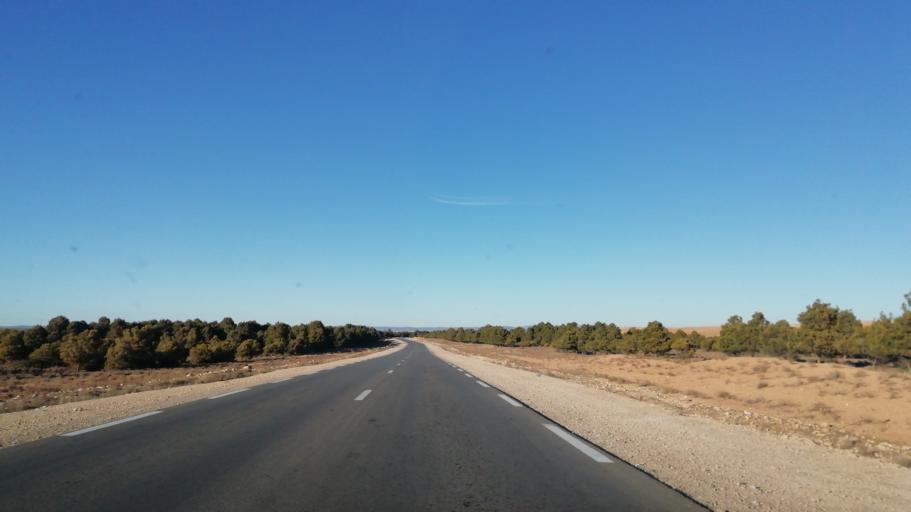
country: DZ
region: Tlemcen
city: Sebdou
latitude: 34.4520
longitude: -1.2753
